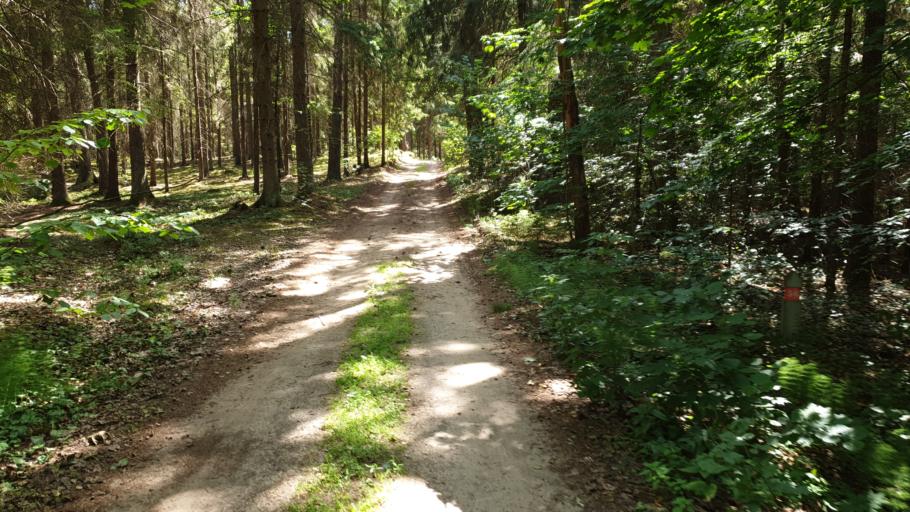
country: LT
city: Grigiskes
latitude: 54.7778
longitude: 24.9932
